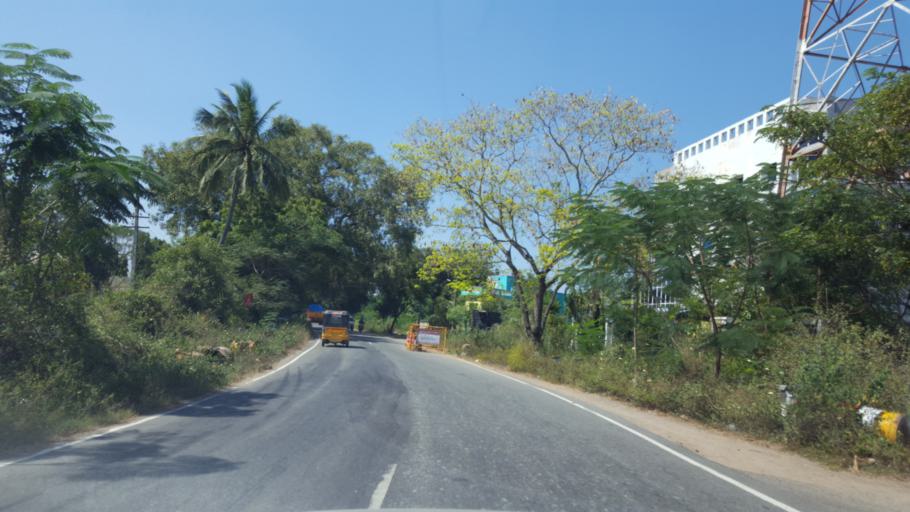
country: IN
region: Tamil Nadu
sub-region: Kancheepuram
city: Chengalpattu
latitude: 12.7355
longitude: 79.9441
